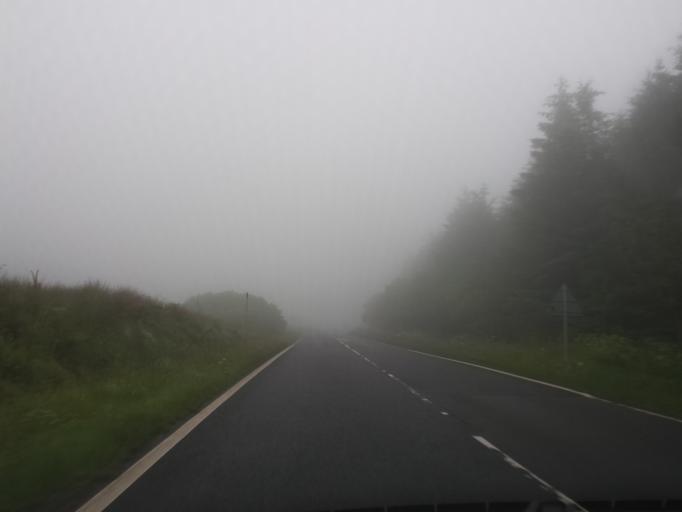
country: GB
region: Scotland
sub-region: Highland
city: Brora
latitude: 58.1634
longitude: -3.5604
